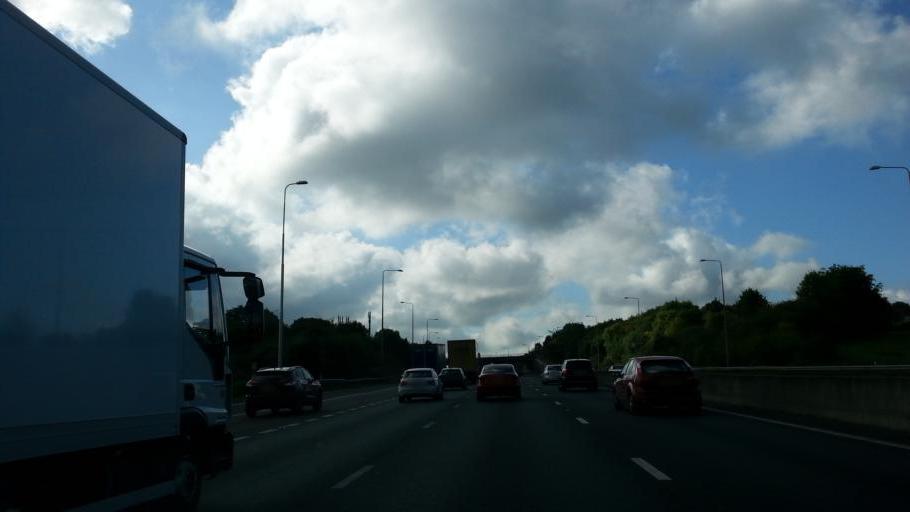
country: GB
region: England
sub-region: Buckinghamshire
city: Gerrards Cross
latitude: 51.5774
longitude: -0.5357
